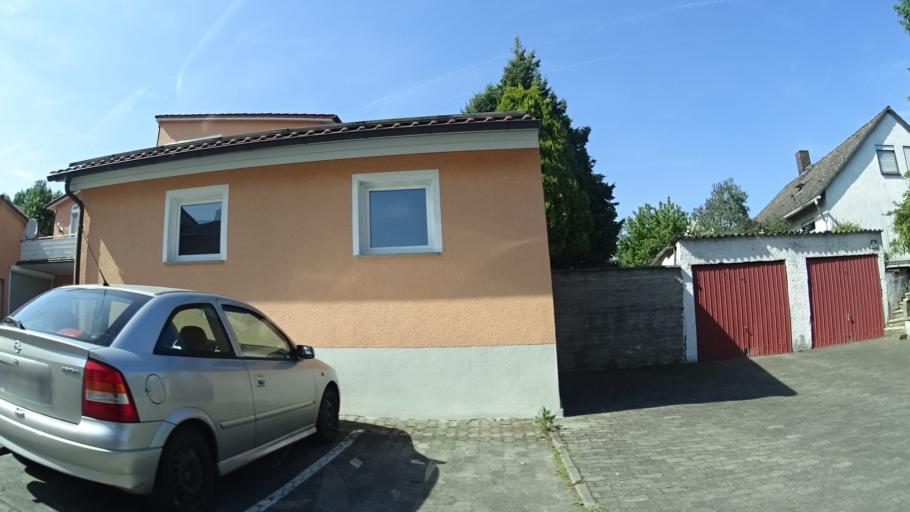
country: DE
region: Hesse
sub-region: Regierungsbezirk Darmstadt
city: Lutzelbach
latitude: 49.7141
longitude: 9.0932
